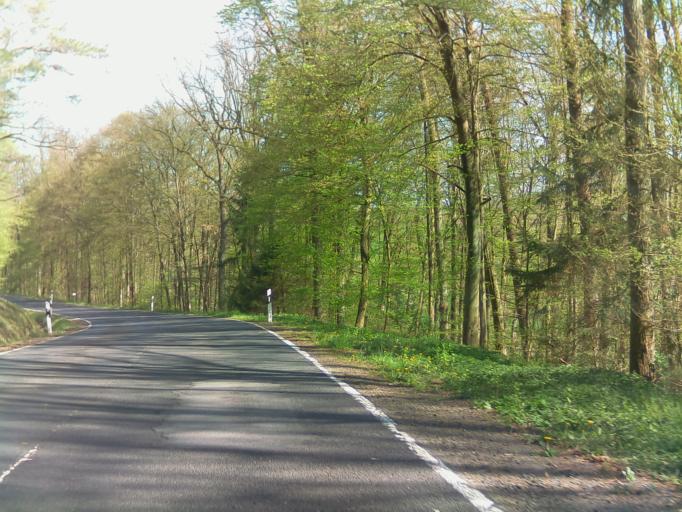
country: DE
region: Bavaria
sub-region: Regierungsbezirk Unterfranken
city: Burgpreppach
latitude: 50.1290
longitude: 10.6182
